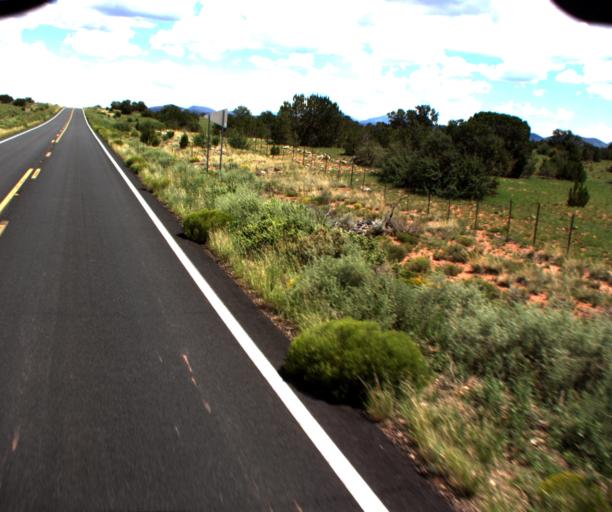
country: US
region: Arizona
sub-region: Coconino County
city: Parks
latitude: 35.6132
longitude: -112.0738
